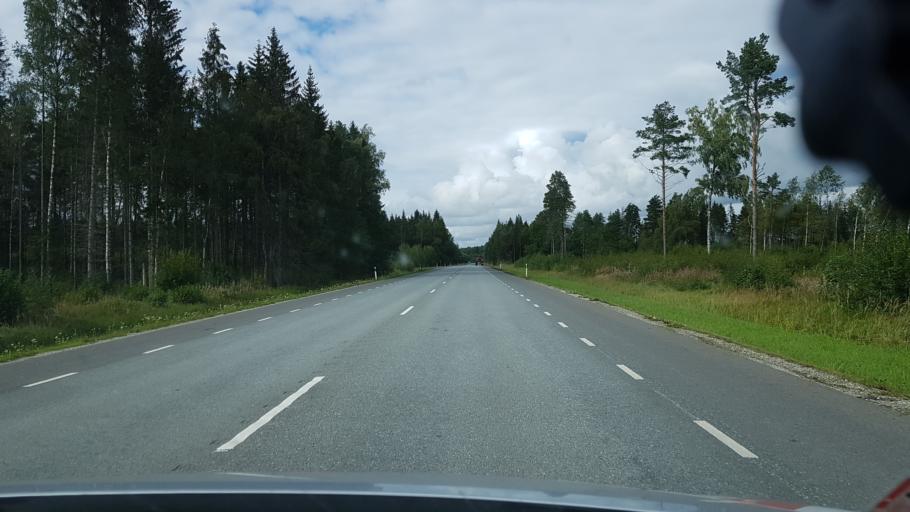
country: EE
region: Raplamaa
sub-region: Kohila vald
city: Kohila
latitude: 59.1543
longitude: 24.7788
